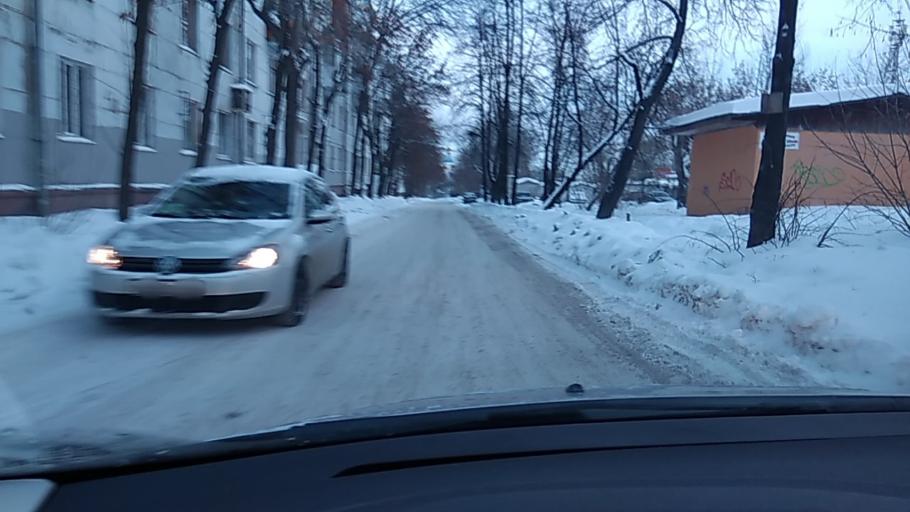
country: RU
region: Sverdlovsk
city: Yekaterinburg
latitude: 56.8884
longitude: 60.5790
